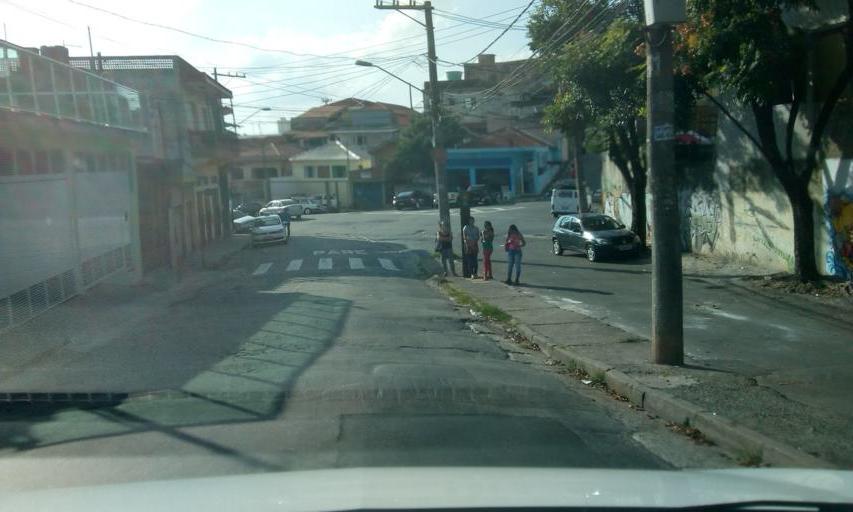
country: BR
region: Sao Paulo
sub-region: Sao Paulo
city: Sao Paulo
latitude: -23.4950
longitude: -46.6833
